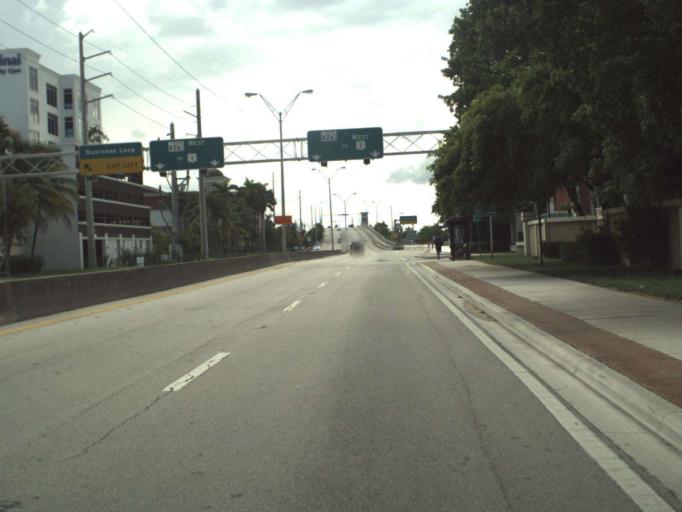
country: US
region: Florida
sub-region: Miami-Dade County
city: Sunny Isles Beach
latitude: 25.9307
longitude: -80.1251
